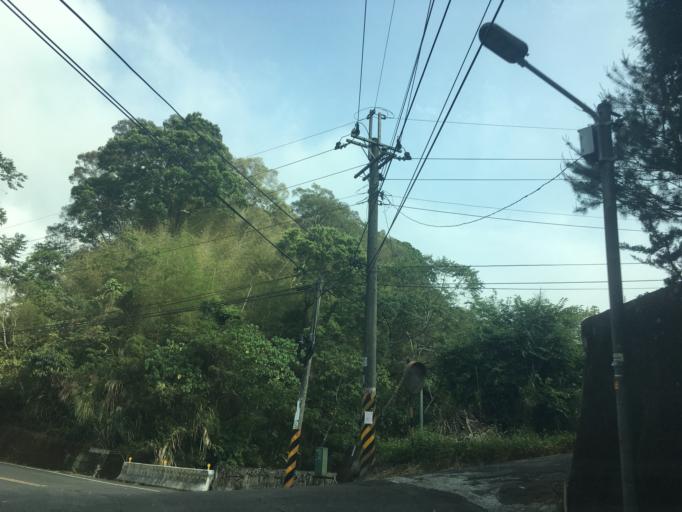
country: TW
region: Taiwan
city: Fengyuan
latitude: 24.2258
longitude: 120.7549
